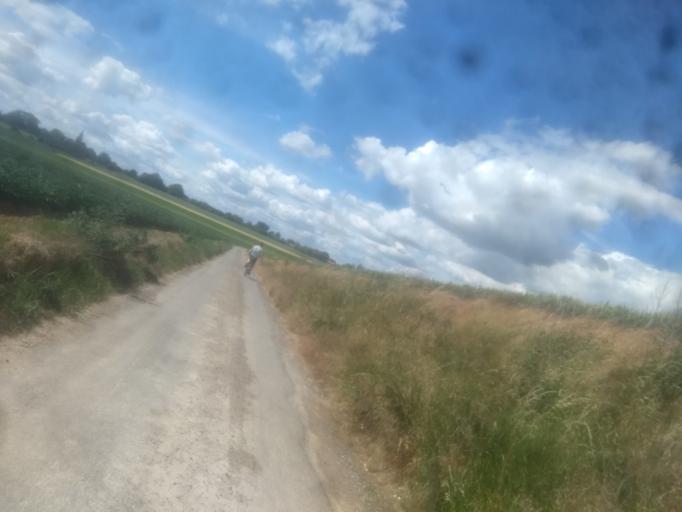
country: FR
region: Nord-Pas-de-Calais
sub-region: Departement du Pas-de-Calais
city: Tilloy-les-Mofflaines
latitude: 50.2422
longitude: 2.8304
